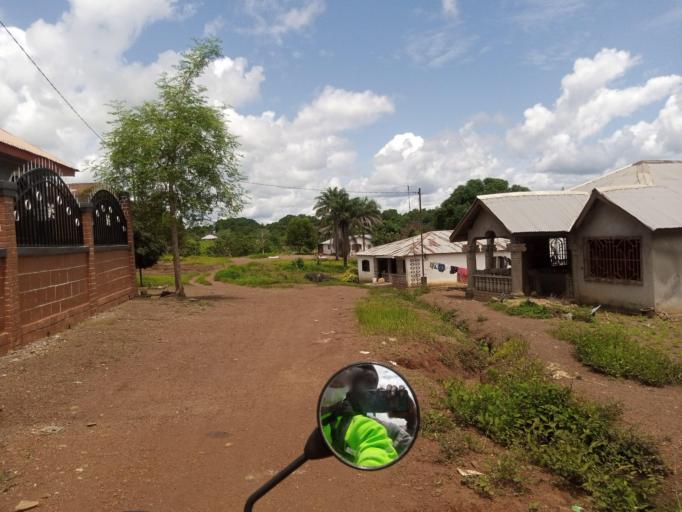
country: SL
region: Northern Province
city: Port Loko
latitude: 8.7577
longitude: -12.7824
